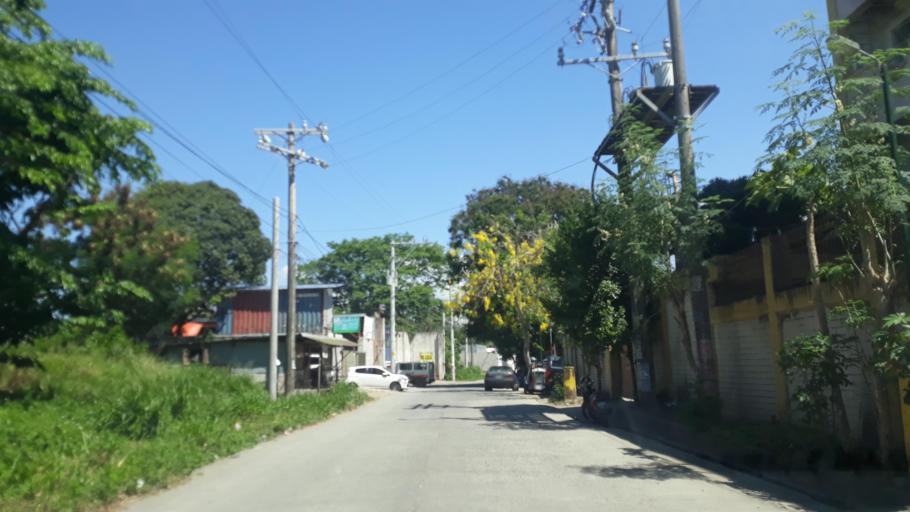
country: PH
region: Calabarzon
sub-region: Province of Cavite
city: Manggahan
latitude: 14.2992
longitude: 120.9169
